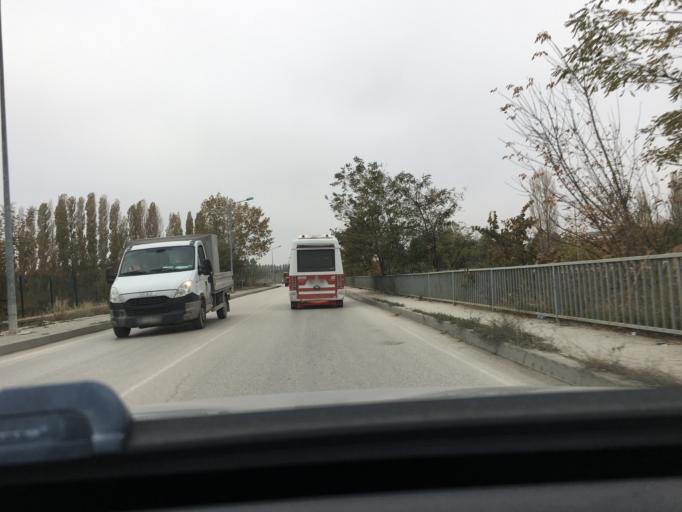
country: TR
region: Eskisehir
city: Eskisehir
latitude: 39.7684
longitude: 30.4798
